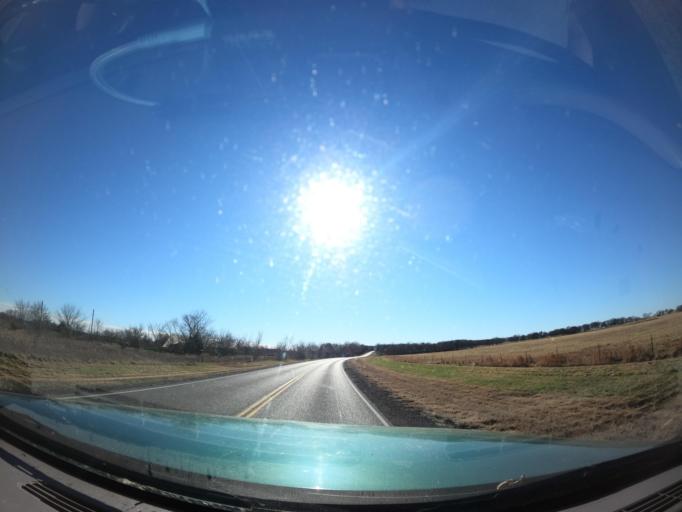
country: US
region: Oklahoma
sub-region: Muskogee County
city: Haskell
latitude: 35.6667
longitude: -95.6429
